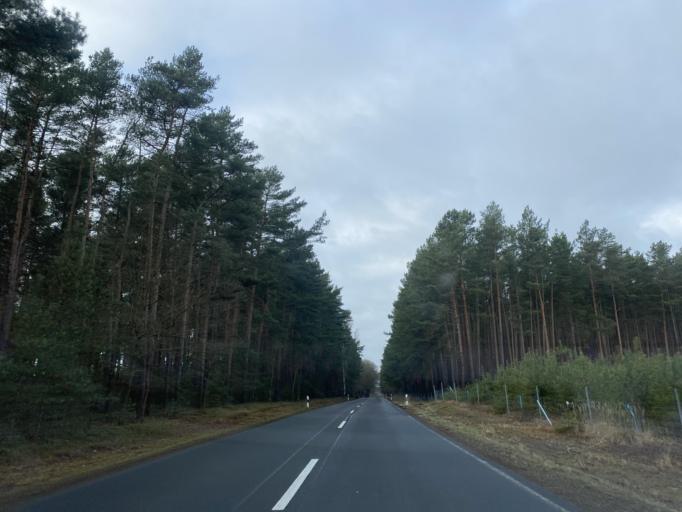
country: PL
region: Lubusz
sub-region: Powiat zarski
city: Leknica
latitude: 51.5075
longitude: 14.7891
